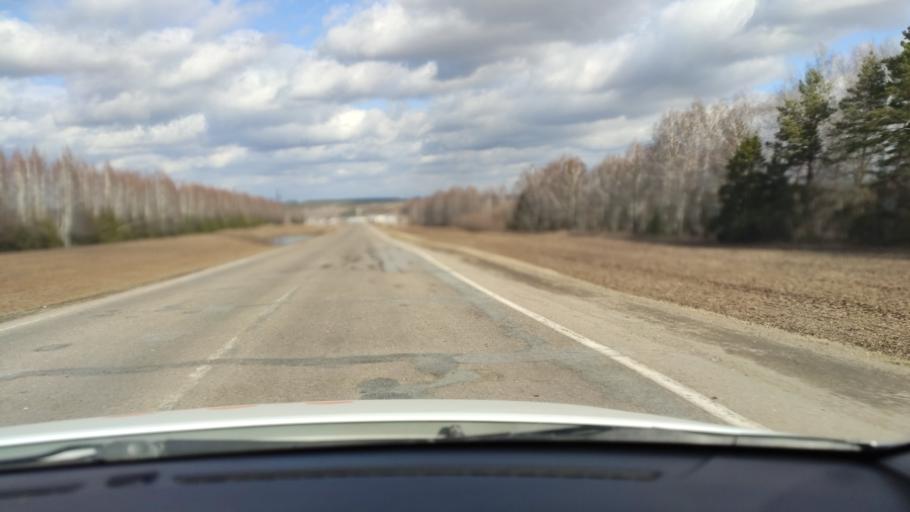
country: RU
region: Tatarstan
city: Vysokaya Gora
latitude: 56.1133
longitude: 49.1879
